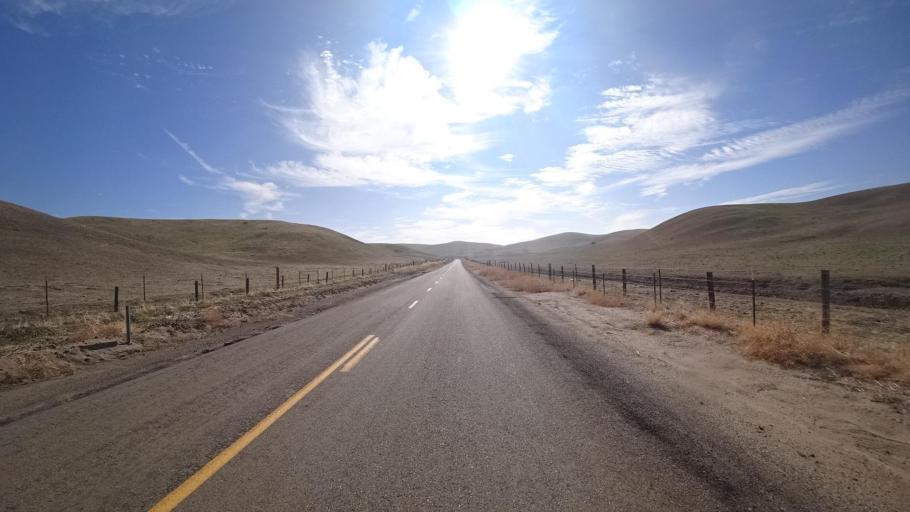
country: US
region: California
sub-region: Kern County
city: Oildale
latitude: 35.6356
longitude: -118.9440
